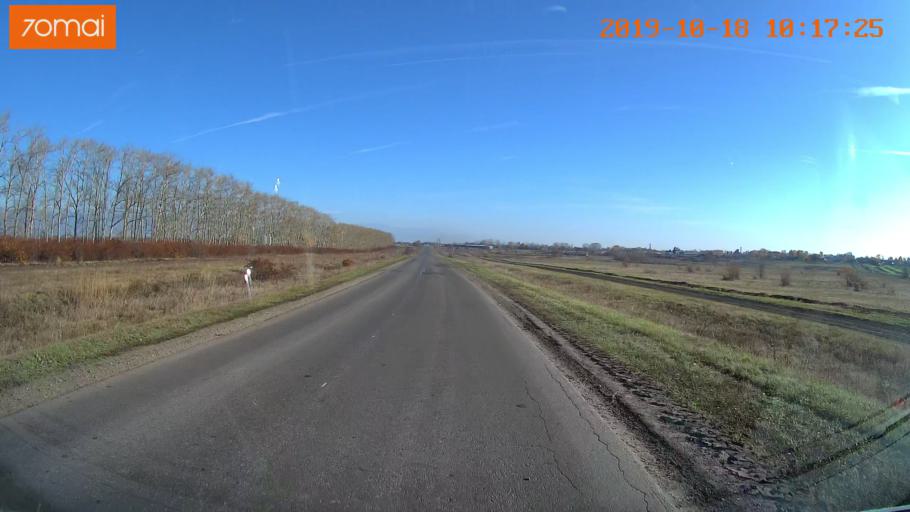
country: RU
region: Tula
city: Kurkino
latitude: 53.4114
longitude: 38.6171
